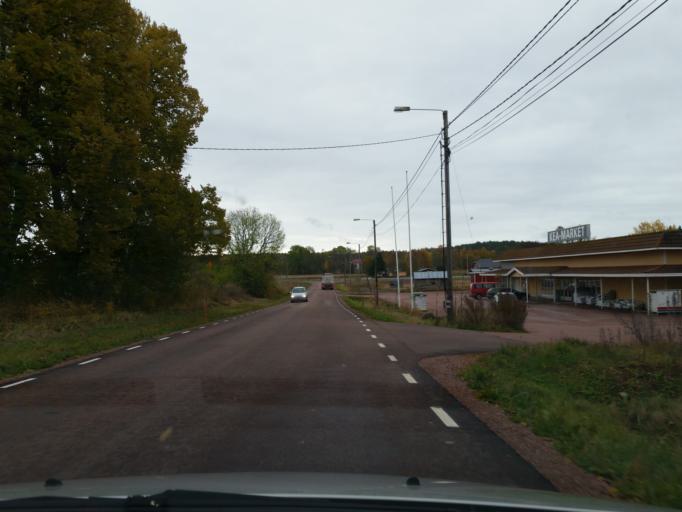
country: AX
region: Alands landsbygd
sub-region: Lemland
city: Lemland
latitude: 60.0714
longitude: 20.0850
